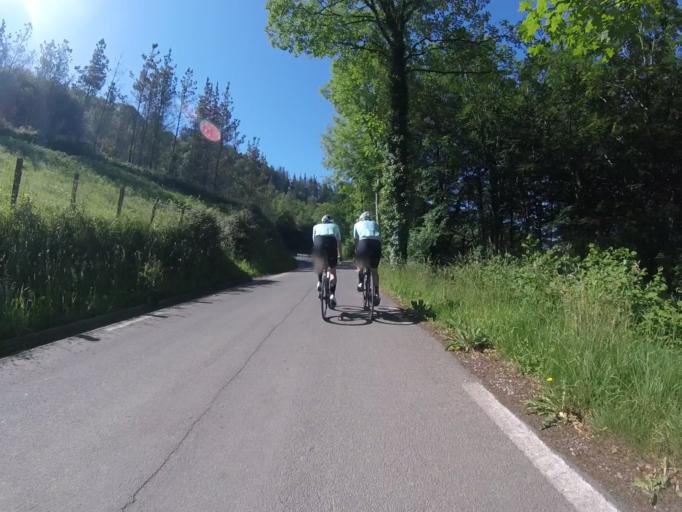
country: ES
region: Basque Country
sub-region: Provincia de Guipuzcoa
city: Beizama
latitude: 43.1280
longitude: -2.1956
